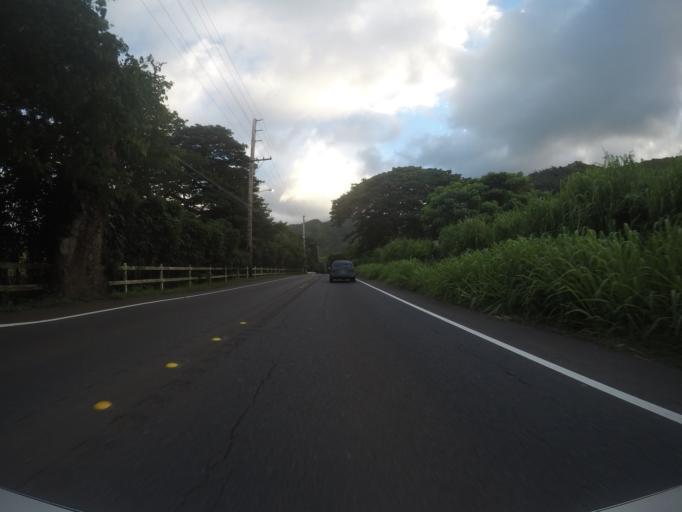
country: US
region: Hawaii
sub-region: Honolulu County
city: Ka'a'awa
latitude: 21.5117
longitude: -157.8509
